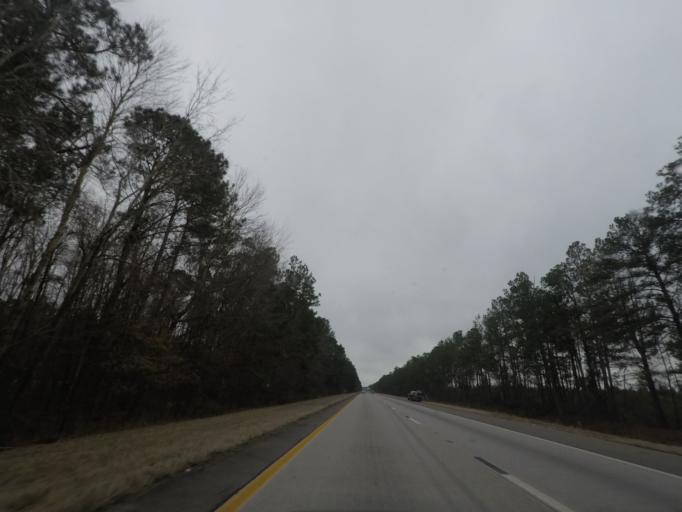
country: US
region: South Carolina
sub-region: Dorchester County
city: Saint George
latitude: 33.0688
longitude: -80.6605
